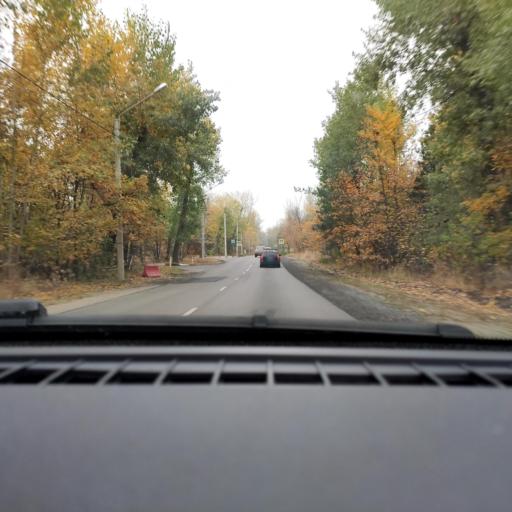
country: RU
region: Voronezj
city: Somovo
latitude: 51.7183
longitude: 39.3226
